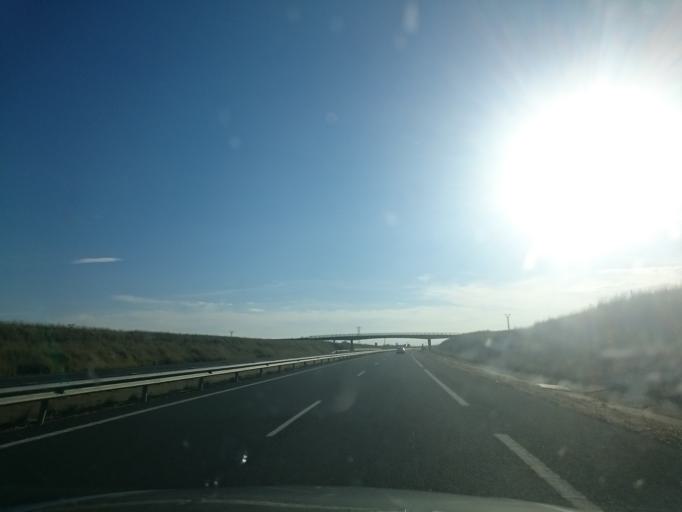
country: ES
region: Castille and Leon
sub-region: Provincia de Palencia
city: Villaherreros
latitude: 42.3929
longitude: -4.4443
